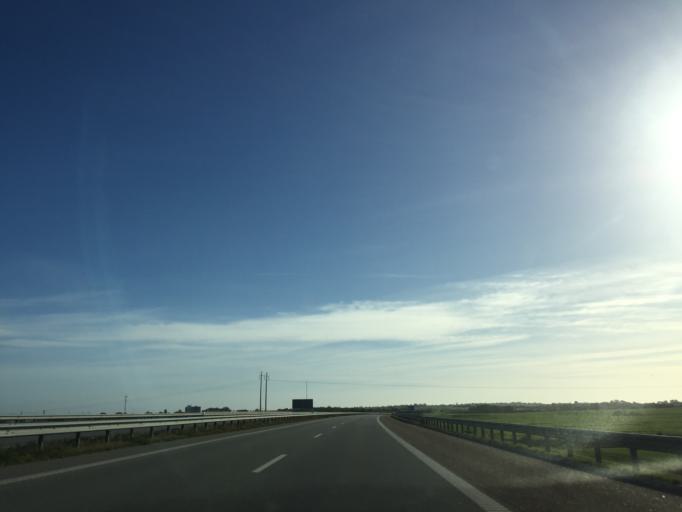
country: DK
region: South Denmark
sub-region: Sonderborg Kommune
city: Dybbol
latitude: 54.9315
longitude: 9.7063
